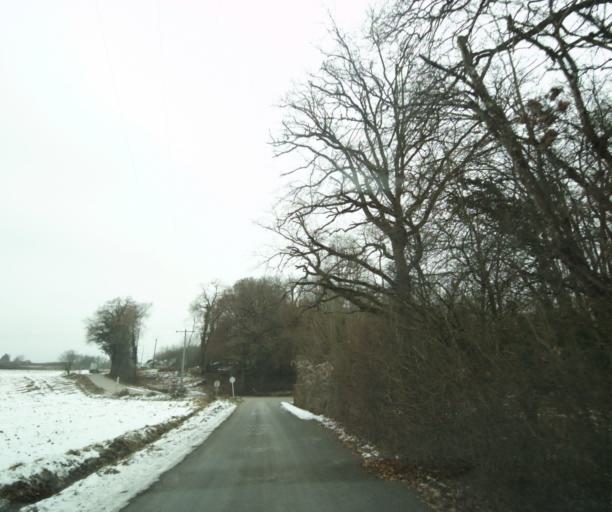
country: FR
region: Rhone-Alpes
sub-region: Departement de la Haute-Savoie
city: Reignier-Esery
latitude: 46.1361
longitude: 6.2960
